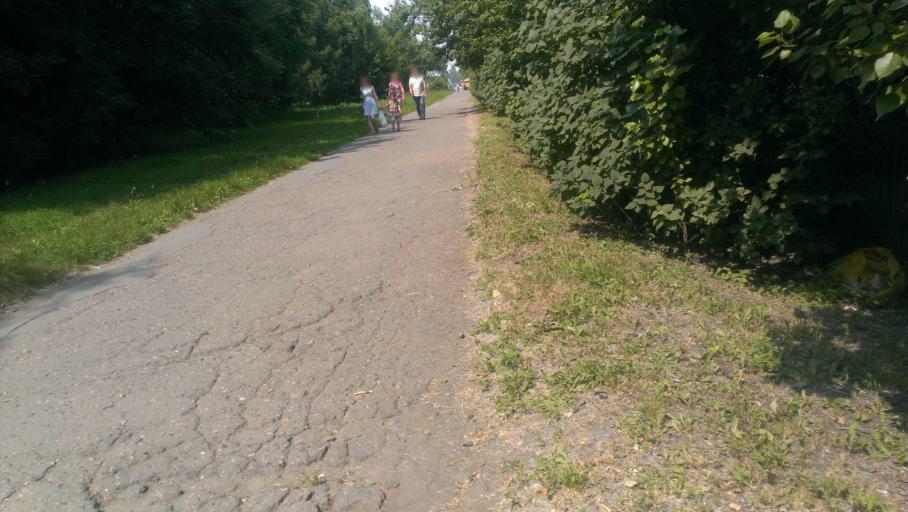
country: RU
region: Altai Krai
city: Novosilikatnyy
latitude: 53.3632
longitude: 83.6753
